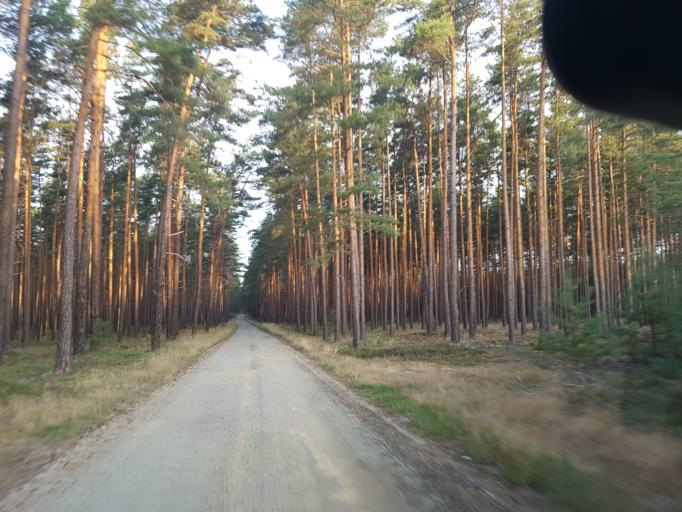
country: DE
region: Brandenburg
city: Schonewalde
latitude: 51.7457
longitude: 13.5620
